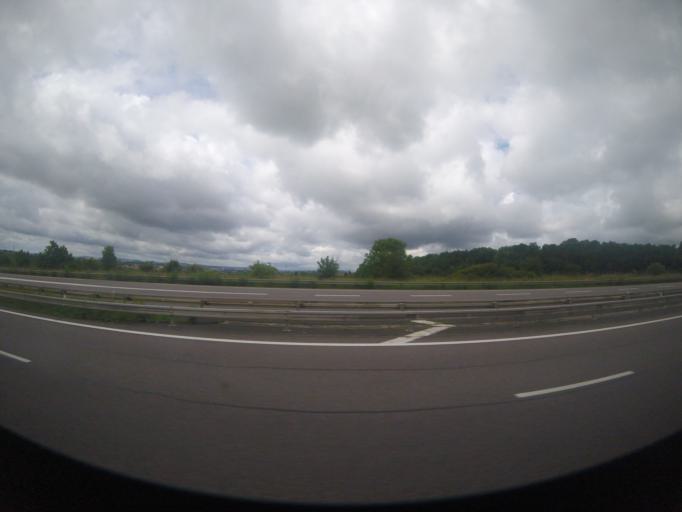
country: FR
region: Lorraine
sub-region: Departement de la Moselle
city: Saint-Julien-les-Metz
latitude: 49.1365
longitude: 6.2470
